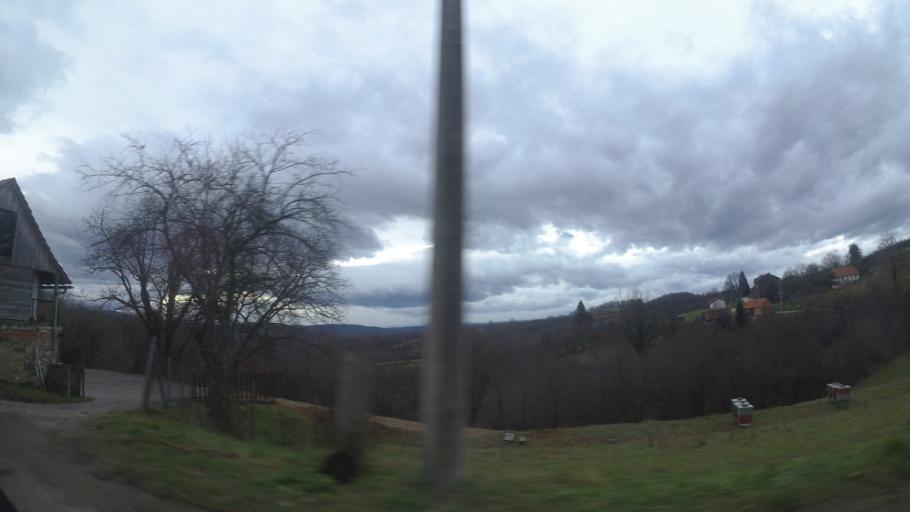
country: HR
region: Karlovacka
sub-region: Grad Karlovac
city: Karlovac
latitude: 45.3903
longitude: 15.5369
